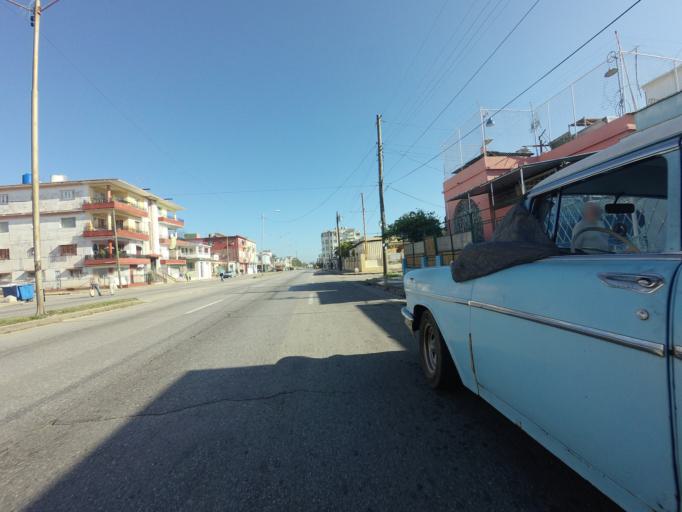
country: CU
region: La Habana
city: Cerro
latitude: 23.1085
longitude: -82.4246
